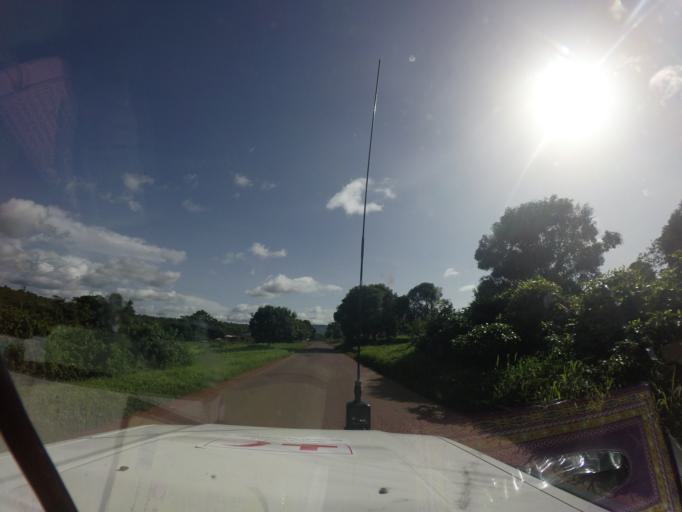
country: GN
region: Mamou
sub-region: Mamou Prefecture
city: Mamou
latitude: 10.2836
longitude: -12.4293
